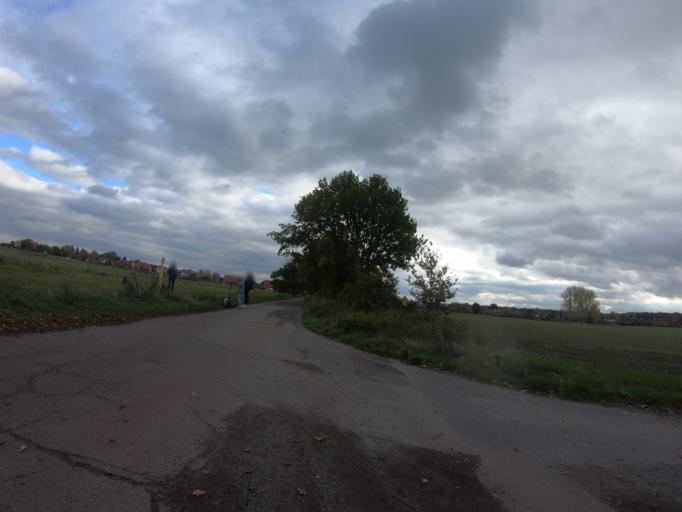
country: DE
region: Lower Saxony
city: Vordorf
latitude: 52.3680
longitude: 10.5126
